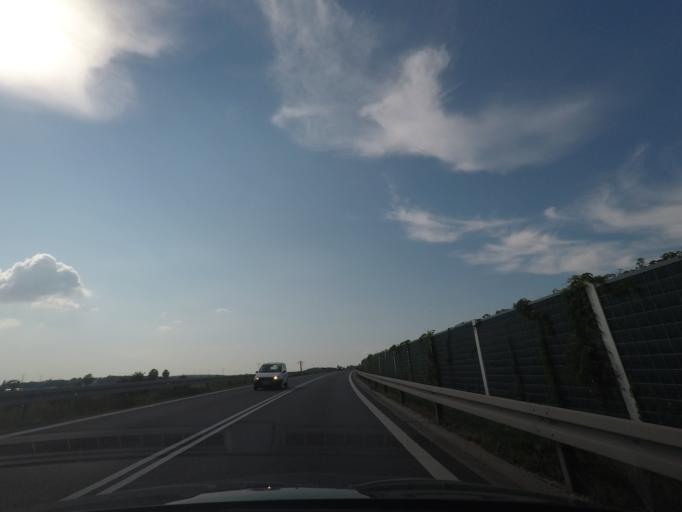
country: PL
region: Silesian Voivodeship
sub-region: Powiat pszczynski
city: Piasek
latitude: 49.9980
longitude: 18.9418
